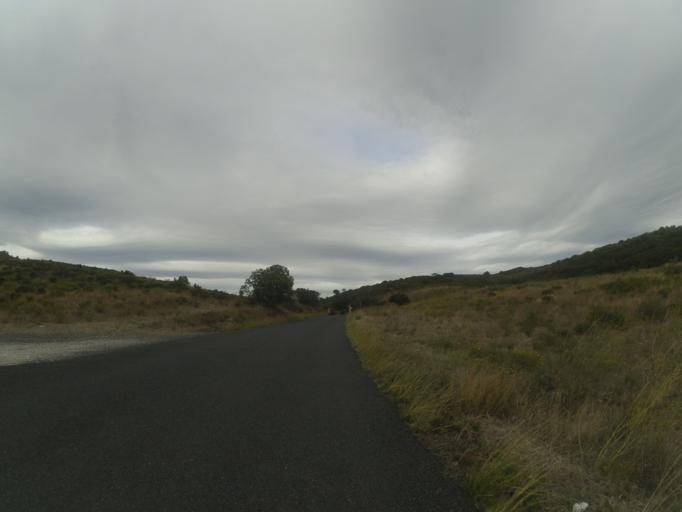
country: FR
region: Languedoc-Roussillon
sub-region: Departement des Pyrenees-Orientales
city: Corneilla-la-Riviere
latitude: 42.7402
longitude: 2.7291
